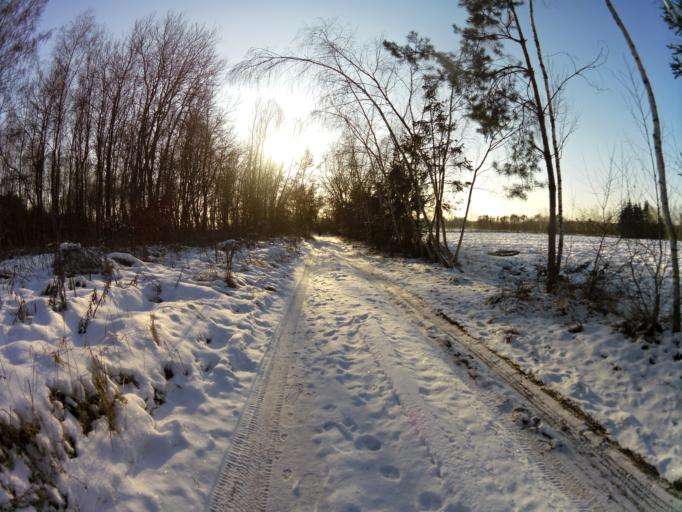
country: PL
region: West Pomeranian Voivodeship
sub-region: Powiat stargardzki
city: Dobrzany
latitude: 53.3394
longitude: 15.4122
